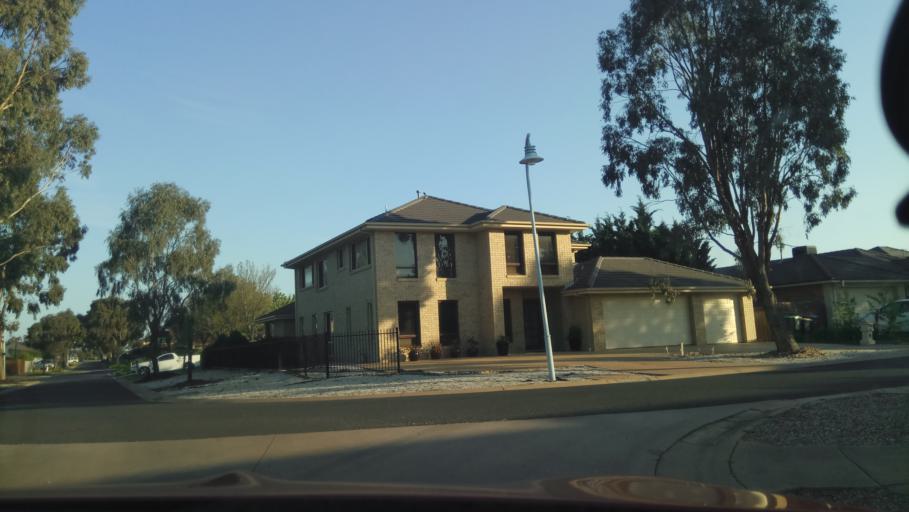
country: AU
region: Victoria
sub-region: Hobsons Bay
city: Altona Meadows
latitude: -37.8891
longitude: 144.7695
